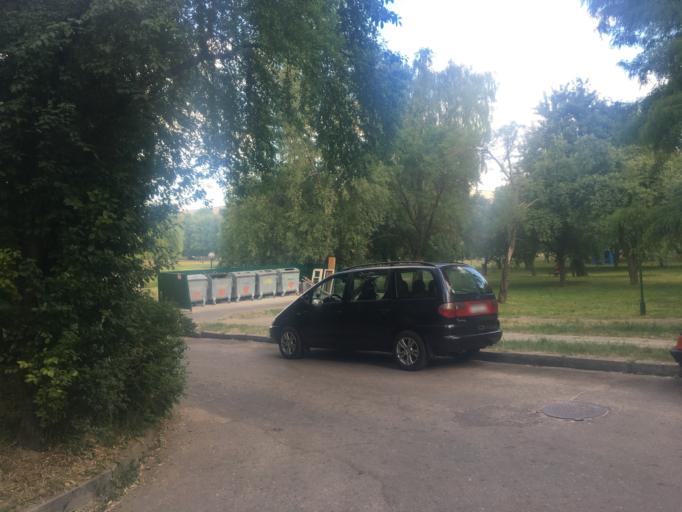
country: BY
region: Grodnenskaya
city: Hrodna
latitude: 53.7050
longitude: 23.8107
